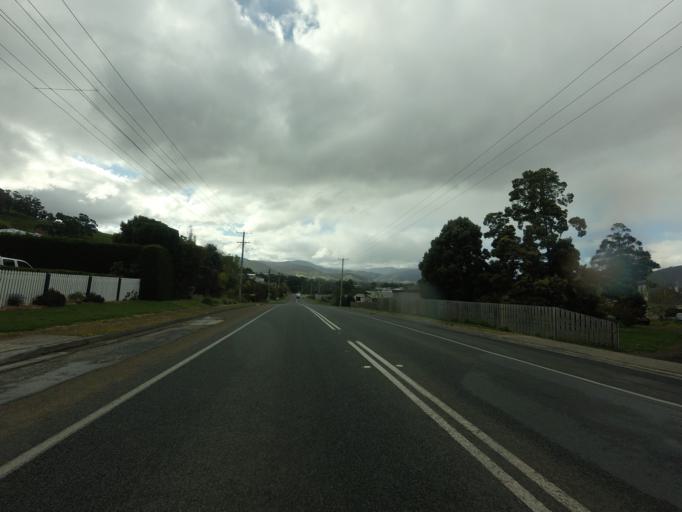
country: AU
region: Tasmania
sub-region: Huon Valley
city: Huonville
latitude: -43.0371
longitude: 147.0462
